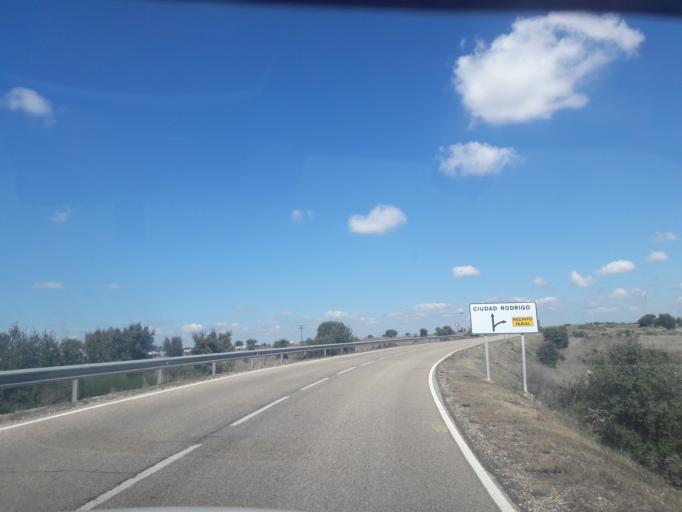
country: ES
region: Castille and Leon
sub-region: Provincia de Salamanca
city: Doninos de Salamanca
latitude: 40.9407
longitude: -5.7258
